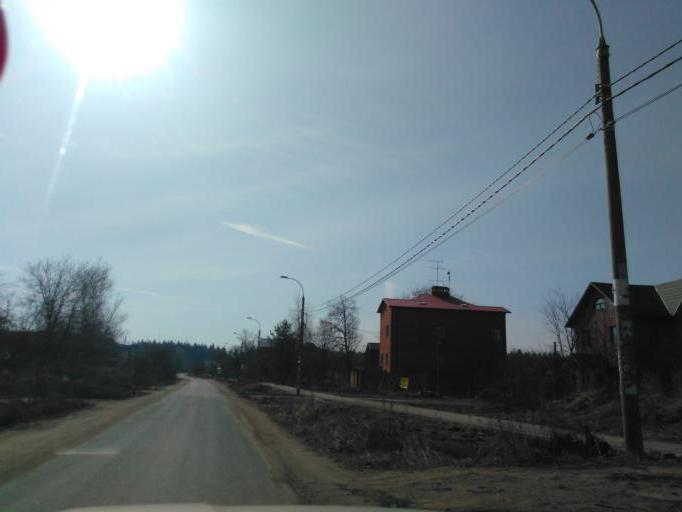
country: RU
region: Moskovskaya
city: Opalikha
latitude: 55.8770
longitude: 37.2682
